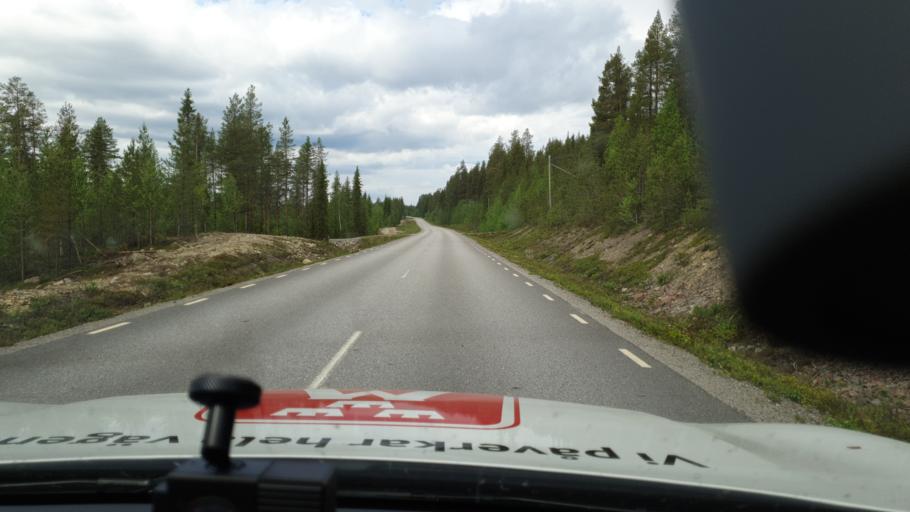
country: SE
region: Vaesterbotten
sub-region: Sorsele Kommun
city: Sorsele
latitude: 65.6859
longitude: 17.2285
